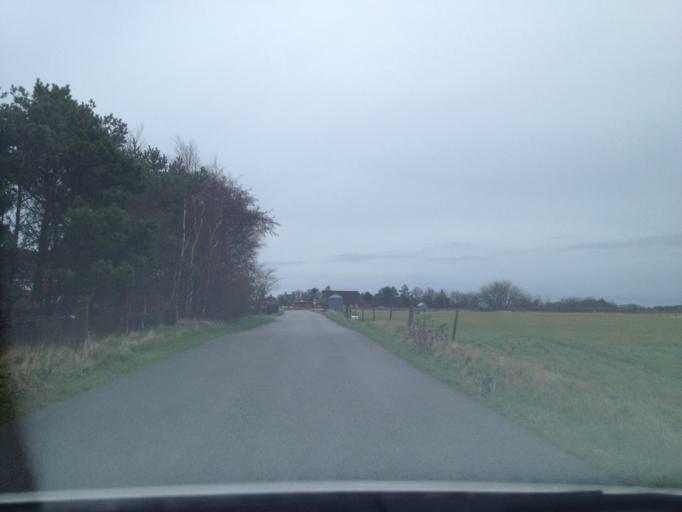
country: DE
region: Schleswig-Holstein
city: List
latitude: 55.1583
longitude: 8.5485
